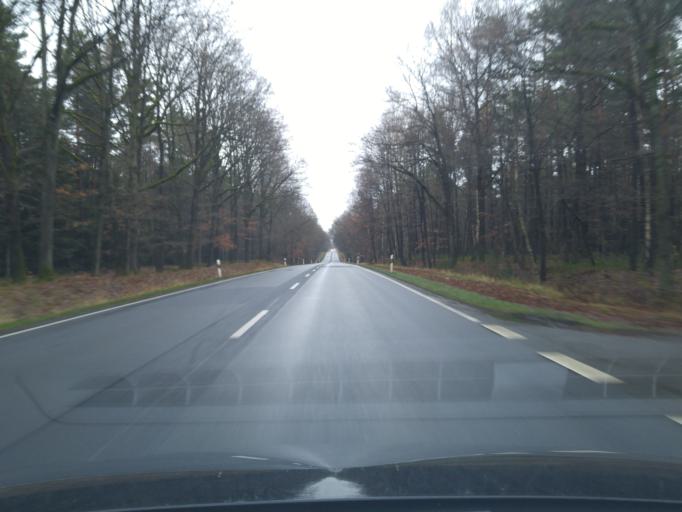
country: DE
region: Lower Saxony
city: Sprakensehl
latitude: 52.7492
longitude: 10.4899
